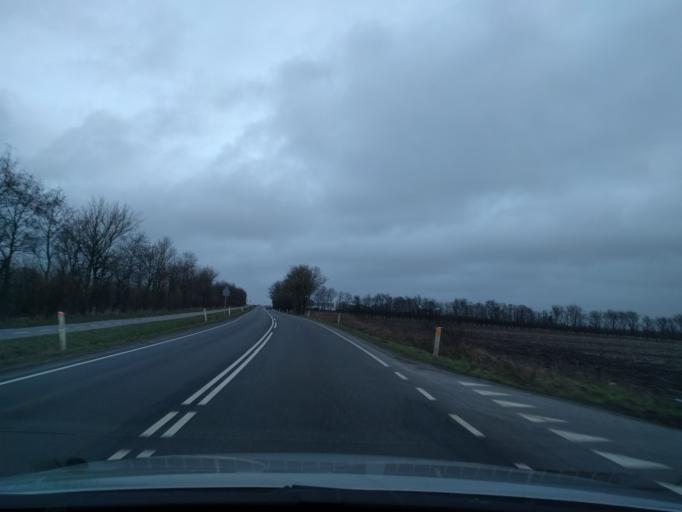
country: DK
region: South Denmark
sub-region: Haderslev Kommune
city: Vojens
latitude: 55.2401
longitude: 9.2326
